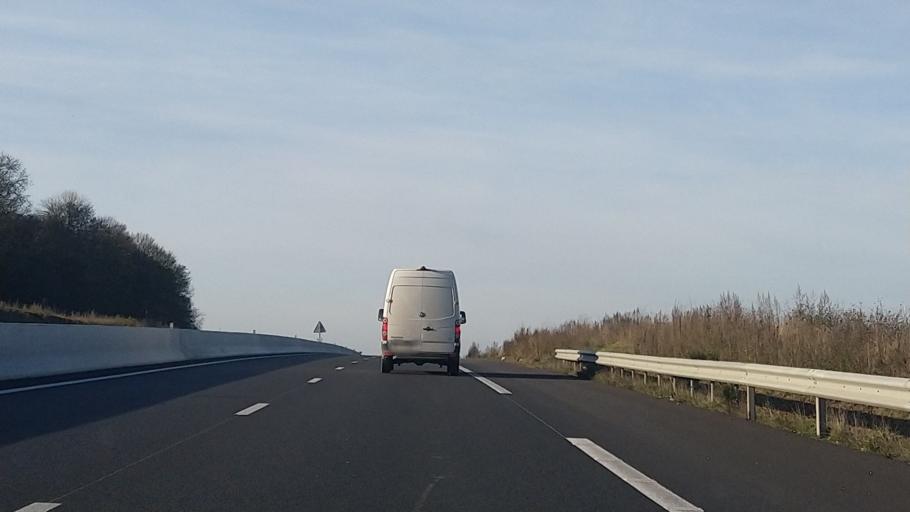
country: FR
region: Ile-de-France
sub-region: Departement du Val-d'Oise
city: Maffliers
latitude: 49.0948
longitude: 2.2986
